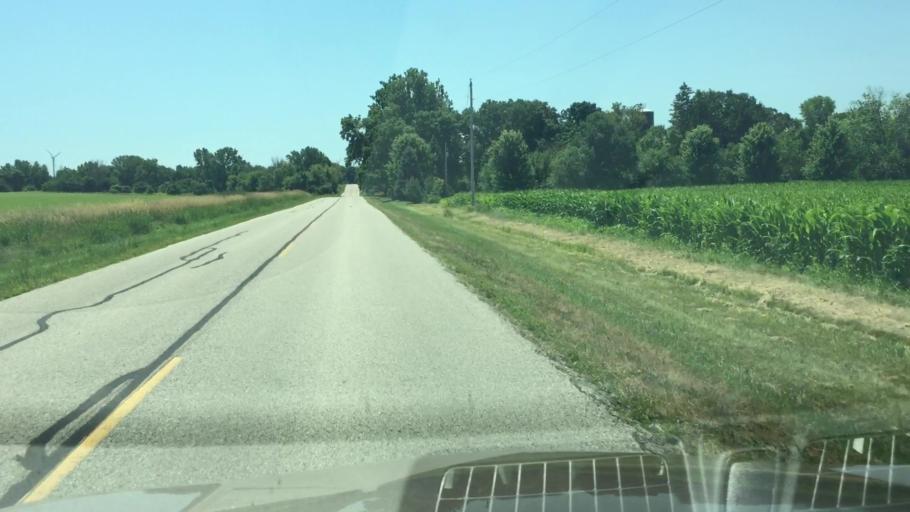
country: US
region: Wisconsin
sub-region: Fond du Lac County
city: Saint Peter
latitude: 43.9436
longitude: -88.3114
